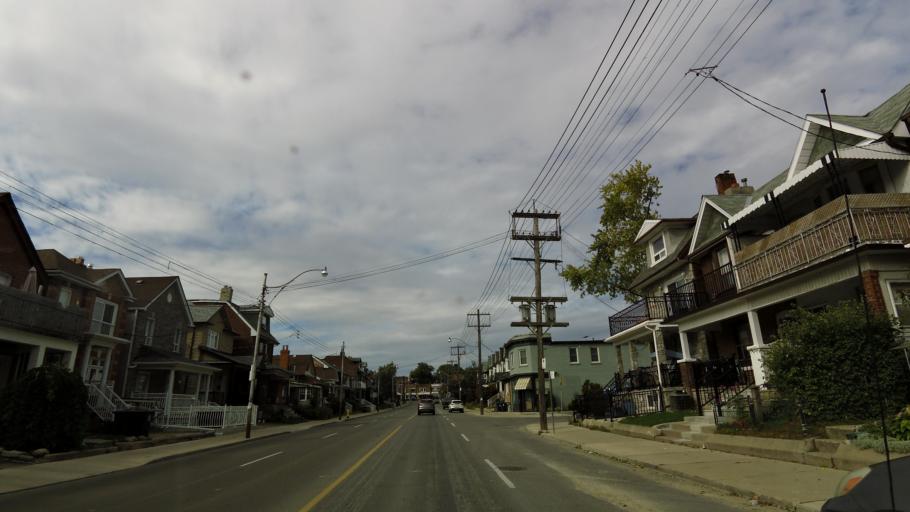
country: CA
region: Ontario
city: Toronto
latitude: 43.6727
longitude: -79.4301
